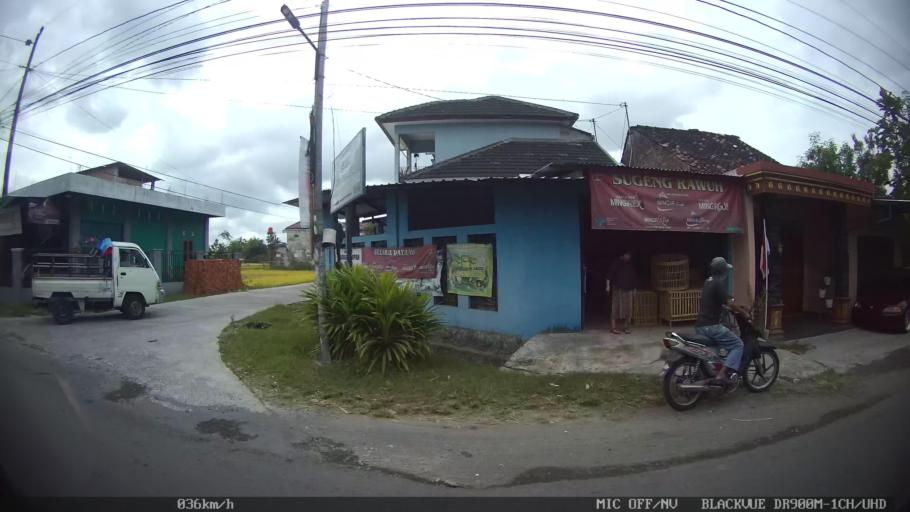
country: ID
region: Daerah Istimewa Yogyakarta
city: Depok
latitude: -7.8310
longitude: 110.4232
